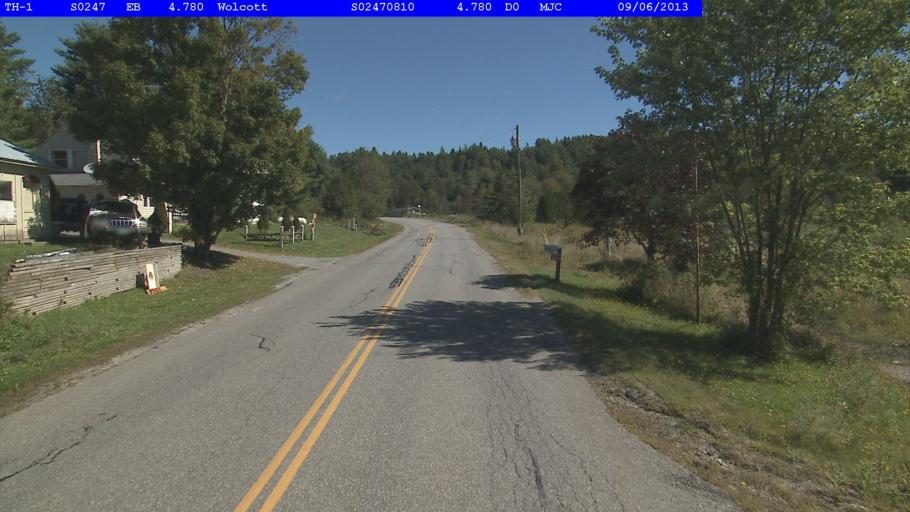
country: US
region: Vermont
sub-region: Caledonia County
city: Hardwick
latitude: 44.6145
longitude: -72.4480
